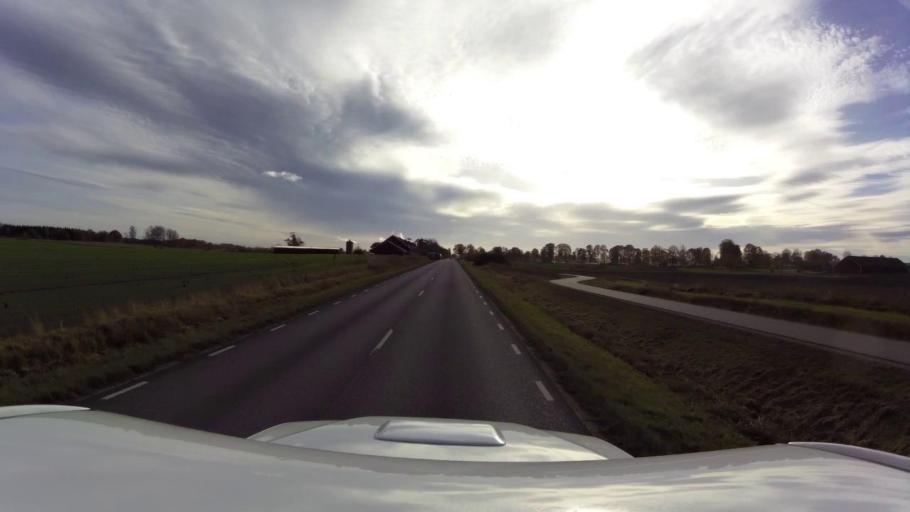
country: SE
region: OEstergoetland
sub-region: Linkopings Kommun
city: Ekangen
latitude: 58.4557
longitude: 15.6413
